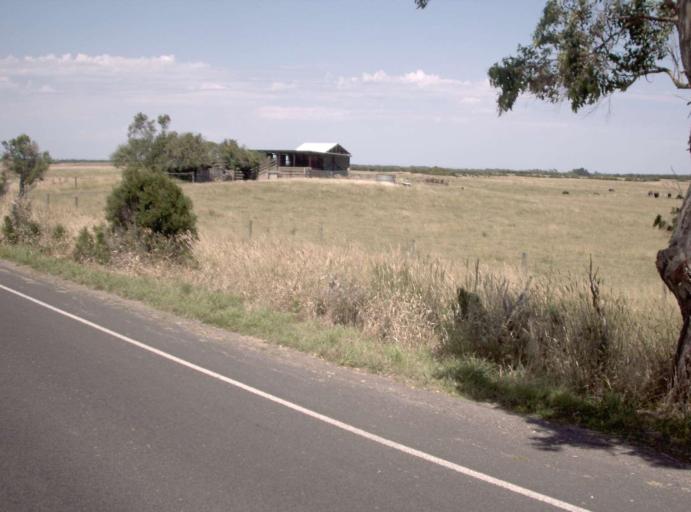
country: AU
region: Victoria
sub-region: Bass Coast
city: North Wonthaggi
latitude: -38.6322
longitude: 145.6035
